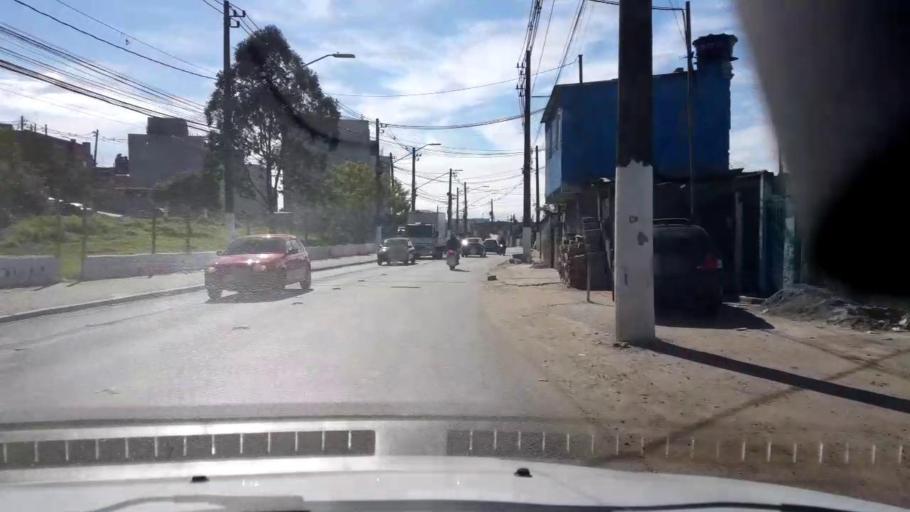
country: BR
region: Sao Paulo
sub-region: Ferraz De Vasconcelos
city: Ferraz de Vasconcelos
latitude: -23.5734
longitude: -46.4159
